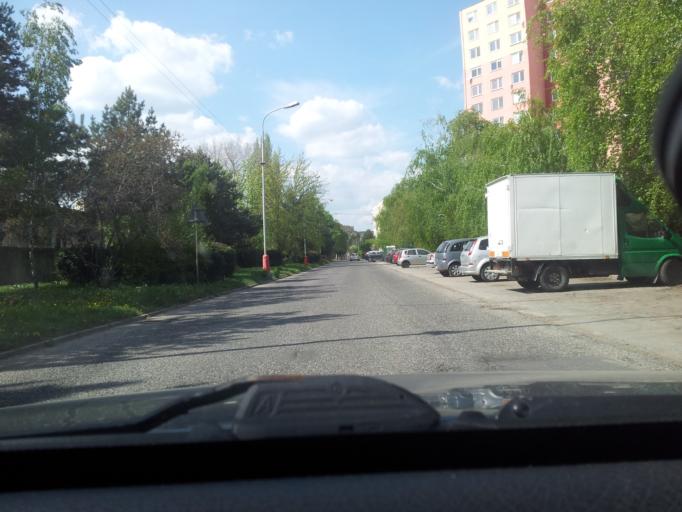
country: SK
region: Nitriansky
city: Levice
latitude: 48.2084
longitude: 18.6007
